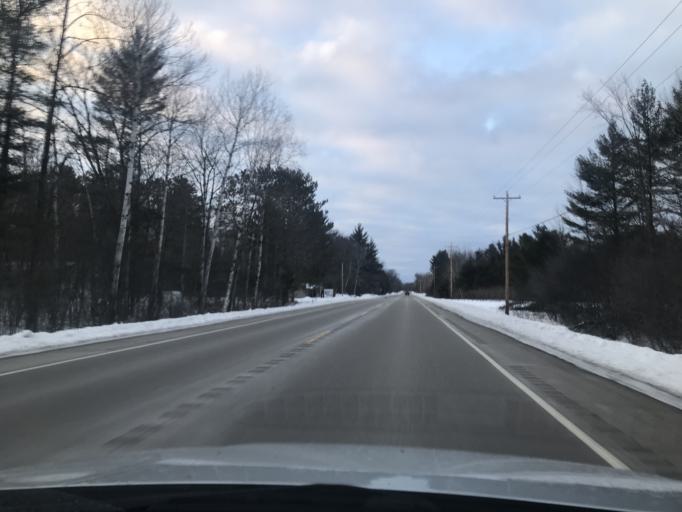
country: US
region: Wisconsin
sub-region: Marinette County
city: Marinette
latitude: 45.1460
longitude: -87.6985
